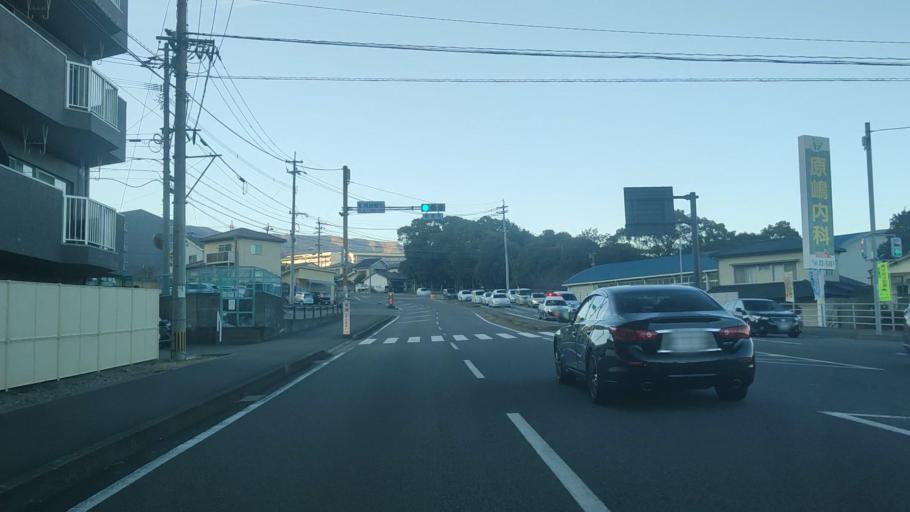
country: JP
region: Oita
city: Beppu
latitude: 33.2878
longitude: 131.4730
